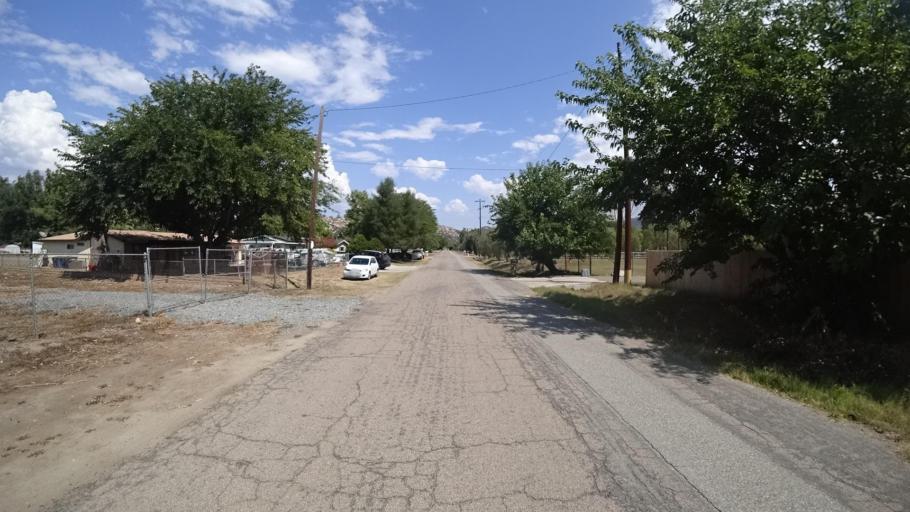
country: US
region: California
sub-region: San Diego County
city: Valley Center
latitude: 33.2096
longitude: -117.0320
